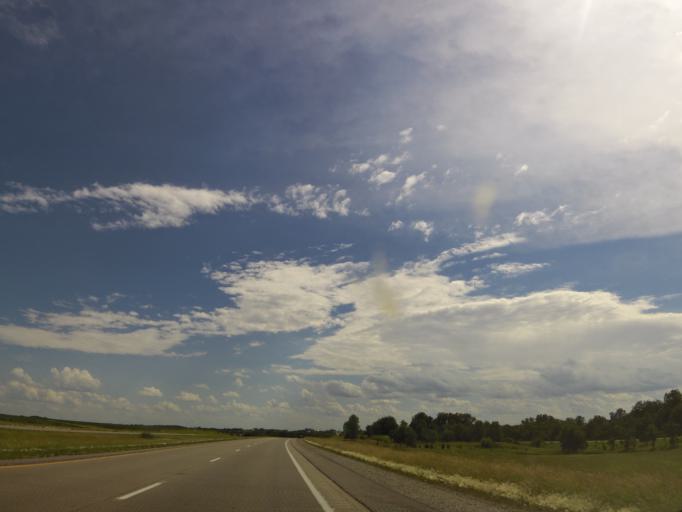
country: US
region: Iowa
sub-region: Henry County
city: Winfield
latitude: 41.1903
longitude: -91.5290
